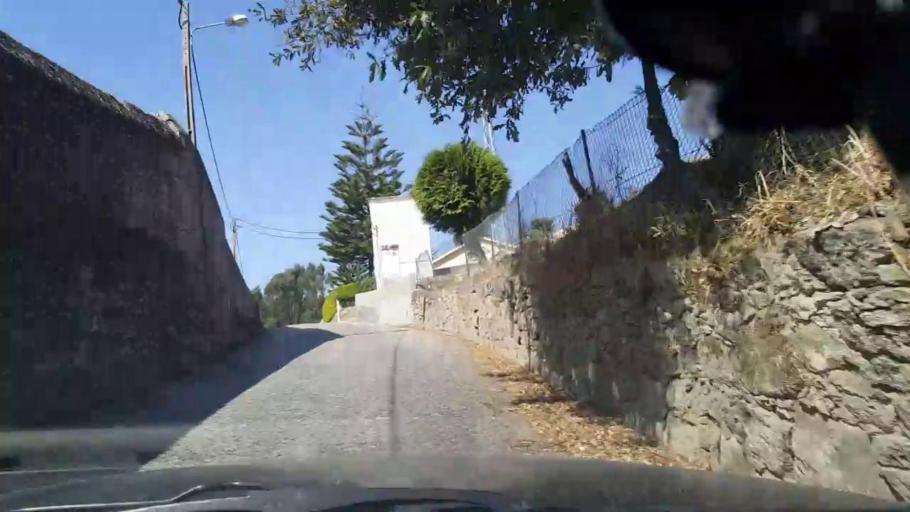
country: PT
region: Porto
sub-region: Vila do Conde
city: Arvore
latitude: 41.3803
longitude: -8.7059
